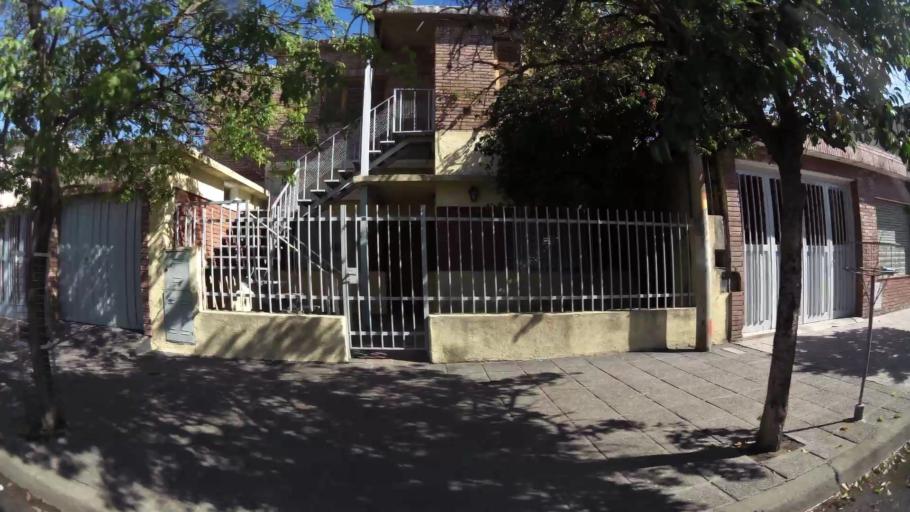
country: AR
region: Cordoba
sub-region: Departamento de Capital
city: Cordoba
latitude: -31.4143
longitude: -64.1513
